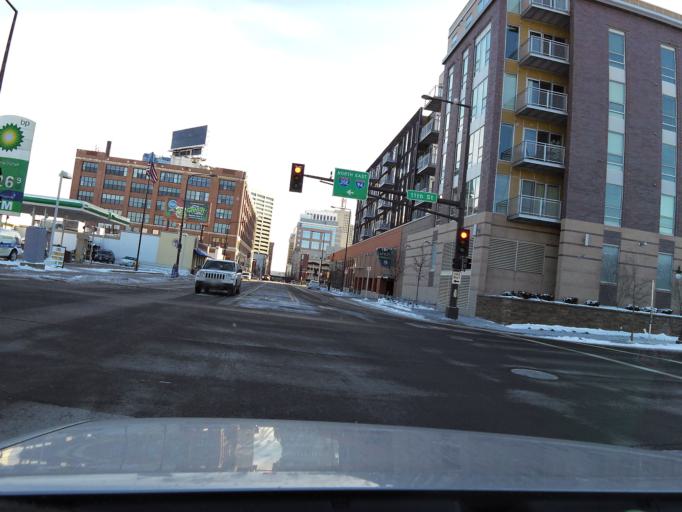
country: US
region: Minnesota
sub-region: Ramsey County
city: Saint Paul
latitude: 44.9522
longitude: -93.0955
